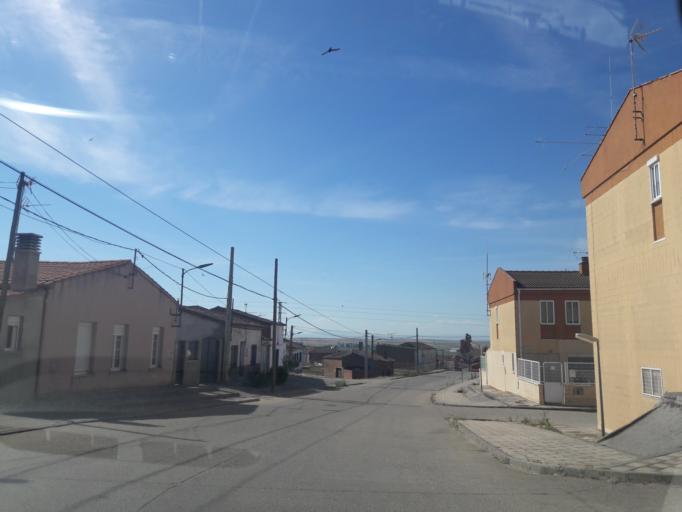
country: ES
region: Castille and Leon
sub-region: Provincia de Salamanca
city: Villoruela
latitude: 41.0115
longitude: -5.3953
